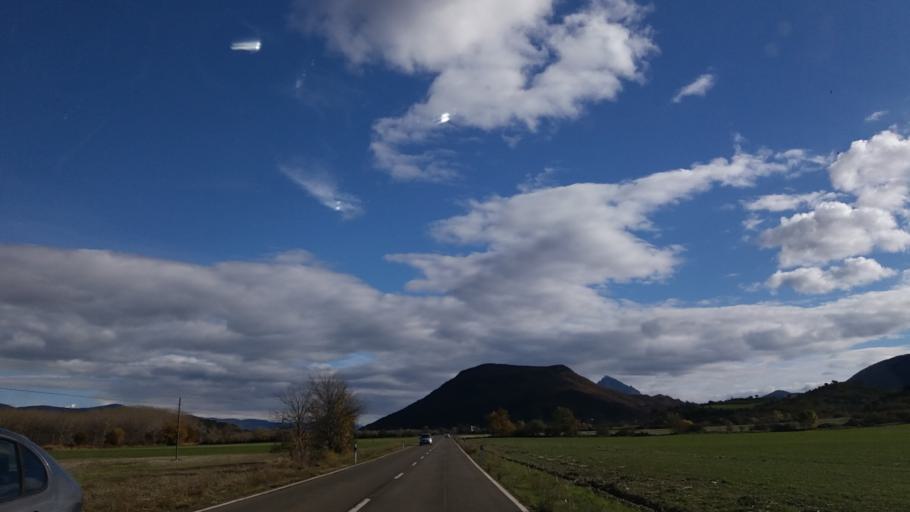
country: ES
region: Aragon
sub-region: Provincia de Huesca
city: Santa Cruz de la Seros
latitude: 42.5568
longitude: -0.6979
